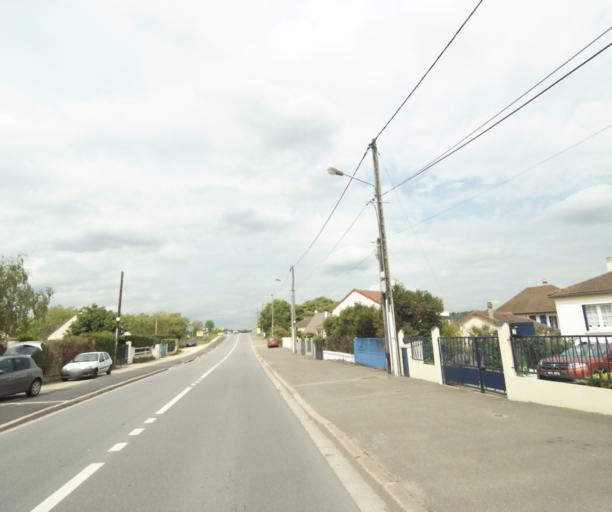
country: FR
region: Ile-de-France
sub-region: Departement des Yvelines
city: Les Mureaux
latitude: 48.9960
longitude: 1.9305
